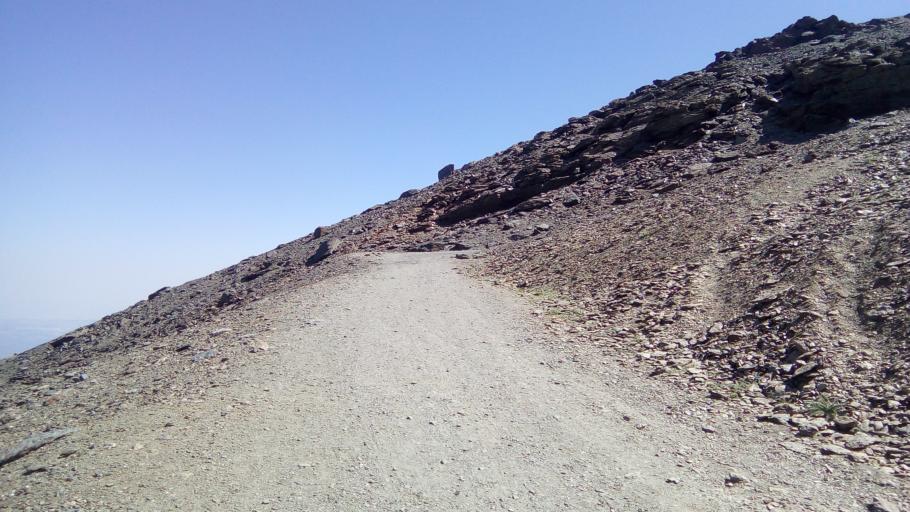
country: ES
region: Andalusia
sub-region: Provincia de Granada
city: Capileira
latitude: 37.0562
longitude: -3.3691
